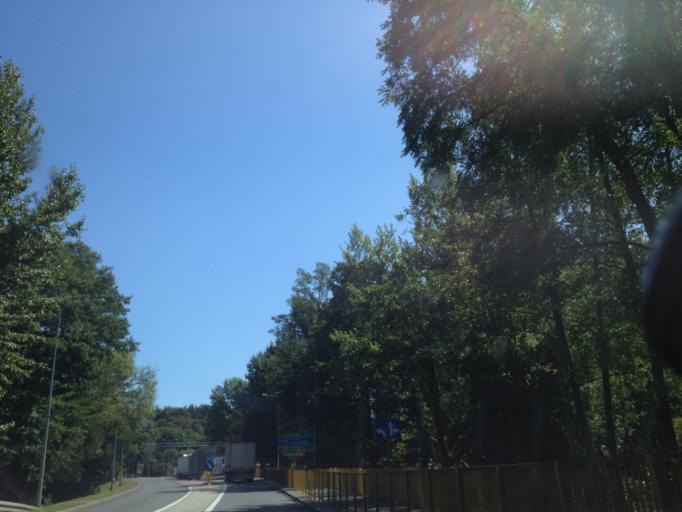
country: PL
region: Lubusz
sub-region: Powiat sulecinski
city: Torzym
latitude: 52.3133
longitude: 15.0792
